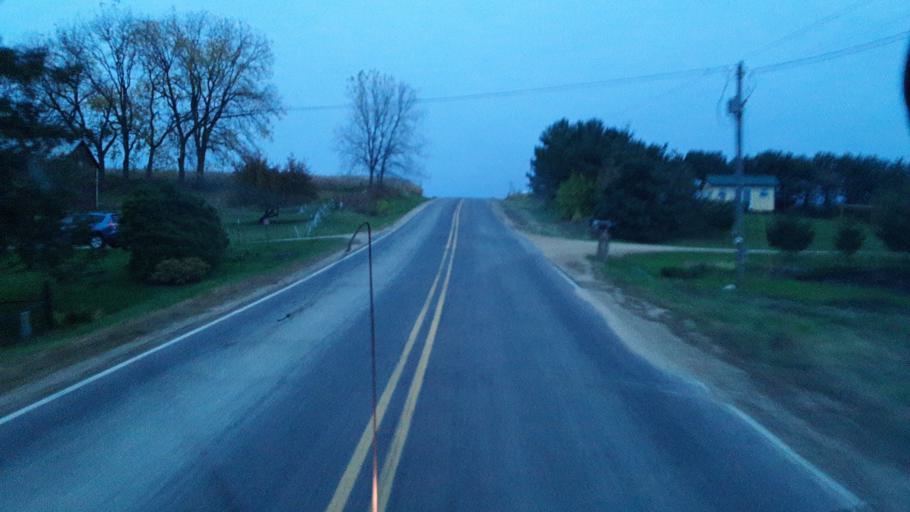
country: US
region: Wisconsin
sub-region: Vernon County
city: Hillsboro
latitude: 43.6590
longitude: -90.4582
